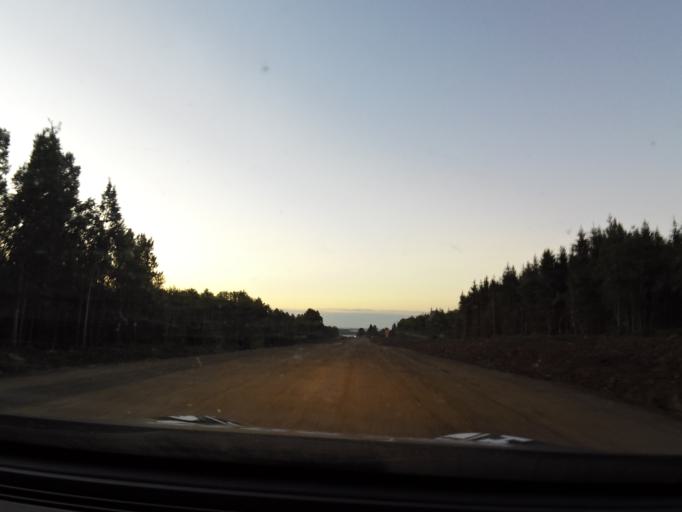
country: RU
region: Vologda
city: Vytegra
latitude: 60.9983
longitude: 36.1246
